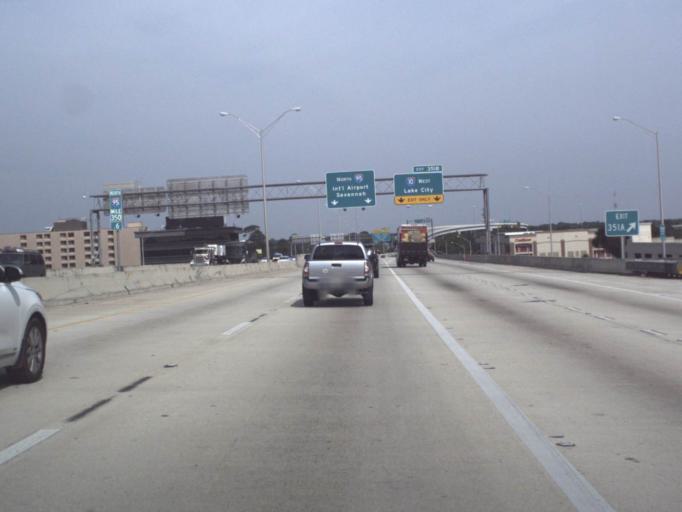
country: US
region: Florida
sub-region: Duval County
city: Jacksonville
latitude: 30.3164
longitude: -81.6753
